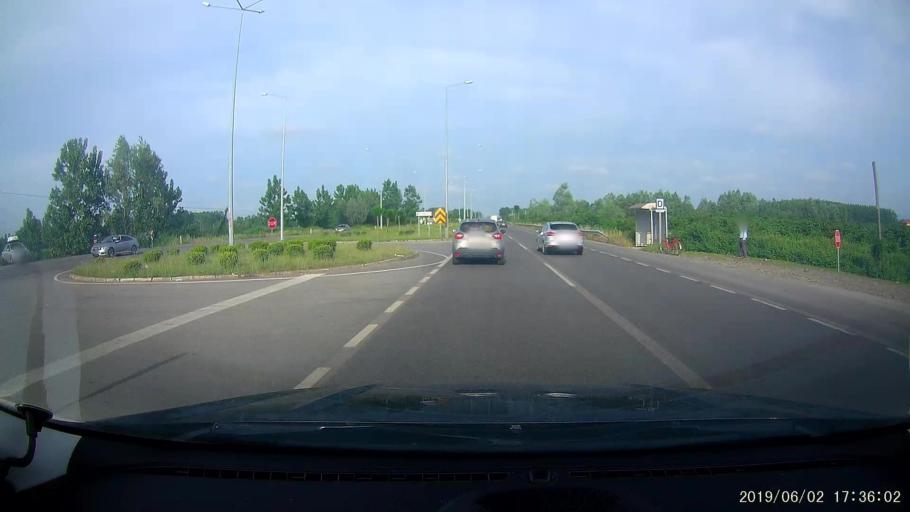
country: TR
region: Samsun
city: Terme
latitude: 41.2191
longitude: 36.8919
